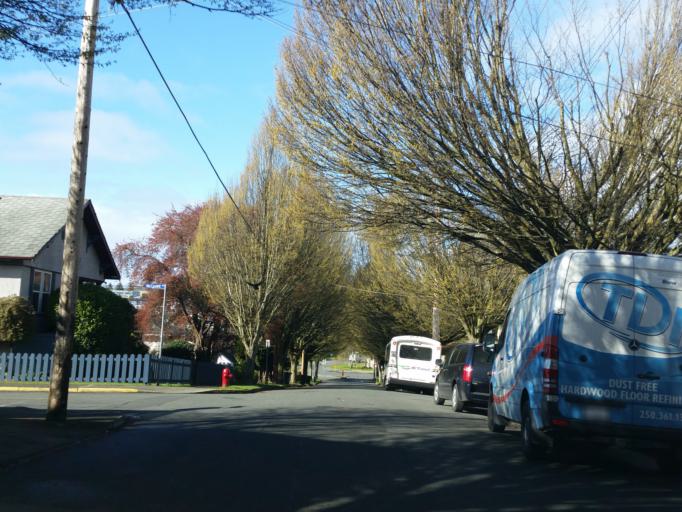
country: CA
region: British Columbia
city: Victoria
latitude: 48.4364
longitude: -123.3920
